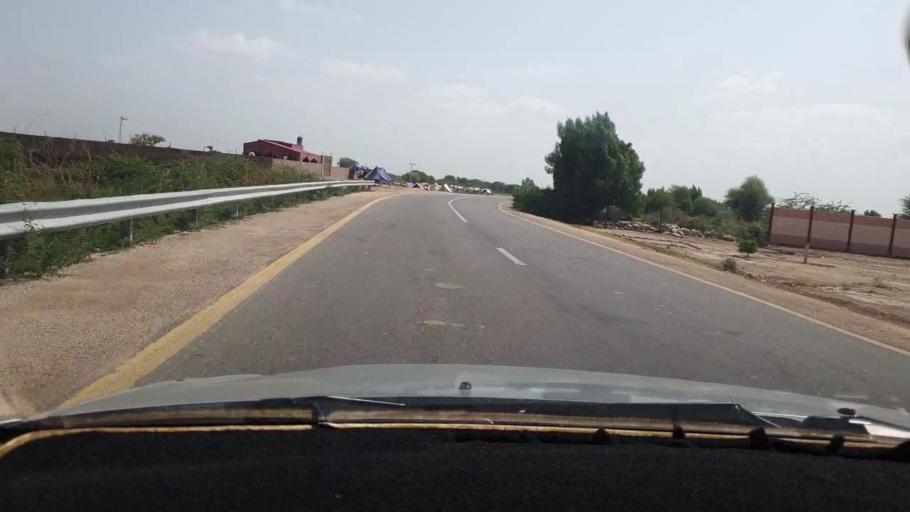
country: PK
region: Sindh
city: Digri
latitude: 25.1502
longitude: 69.1259
